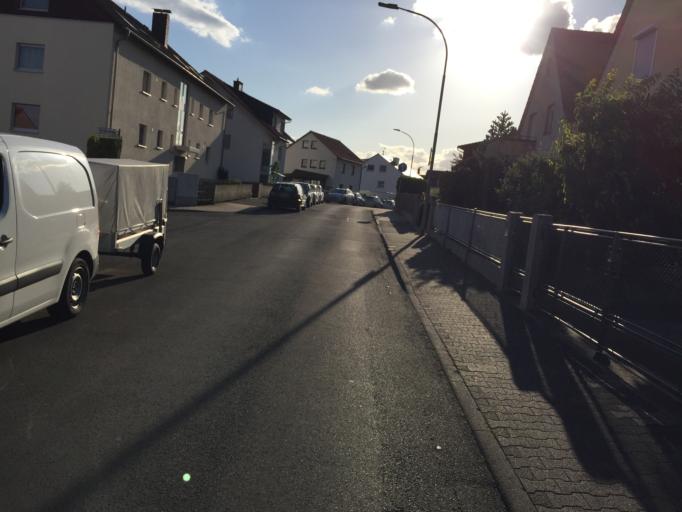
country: DE
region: Hesse
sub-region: Regierungsbezirk Darmstadt
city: Niederdorfelden
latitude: 50.2130
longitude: 8.7872
